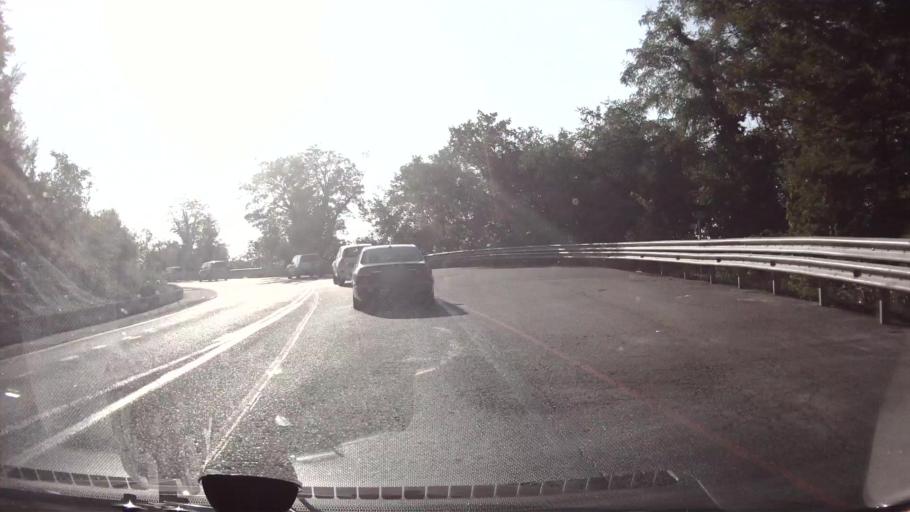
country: RU
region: Krasnodarskiy
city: Shepsi
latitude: 44.0540
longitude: 39.1310
